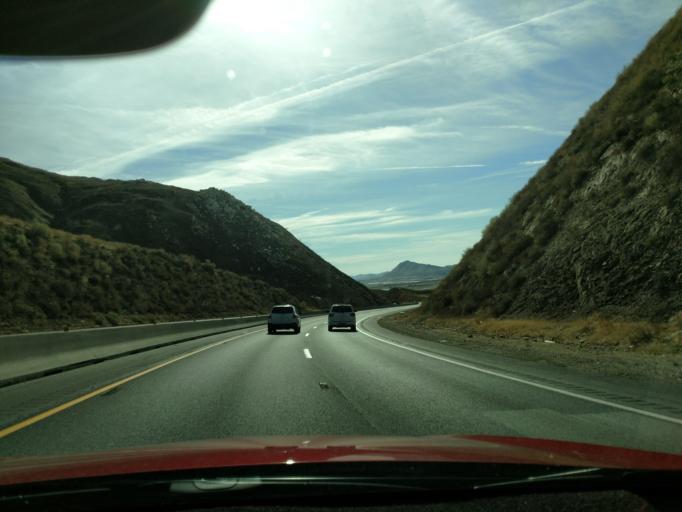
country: US
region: California
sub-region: Riverside County
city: Beaumont
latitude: 33.8626
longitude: -117.0079
